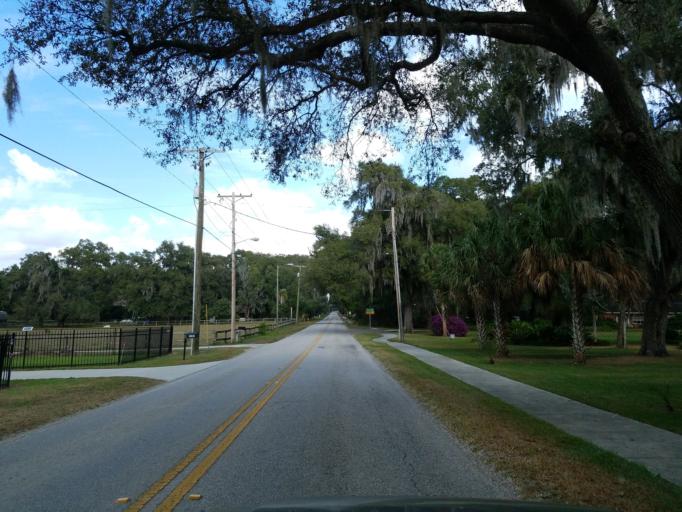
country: US
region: Florida
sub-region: Hillsborough County
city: Bloomingdale
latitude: 27.8995
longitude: -82.2198
